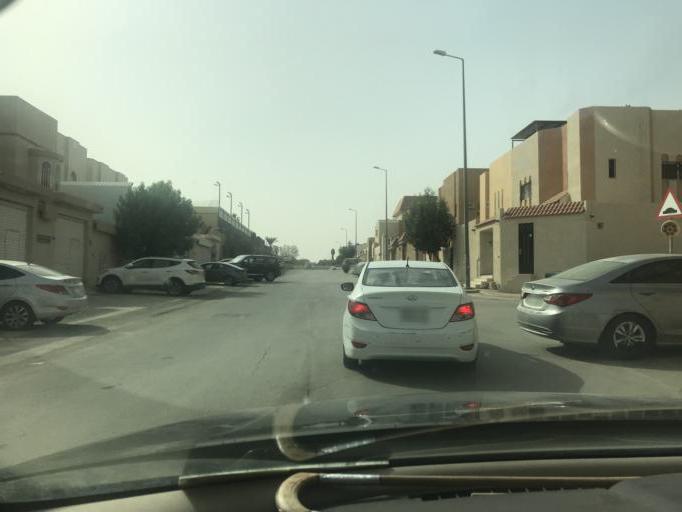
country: SA
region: Ar Riyad
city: Riyadh
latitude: 24.7572
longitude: 46.7680
